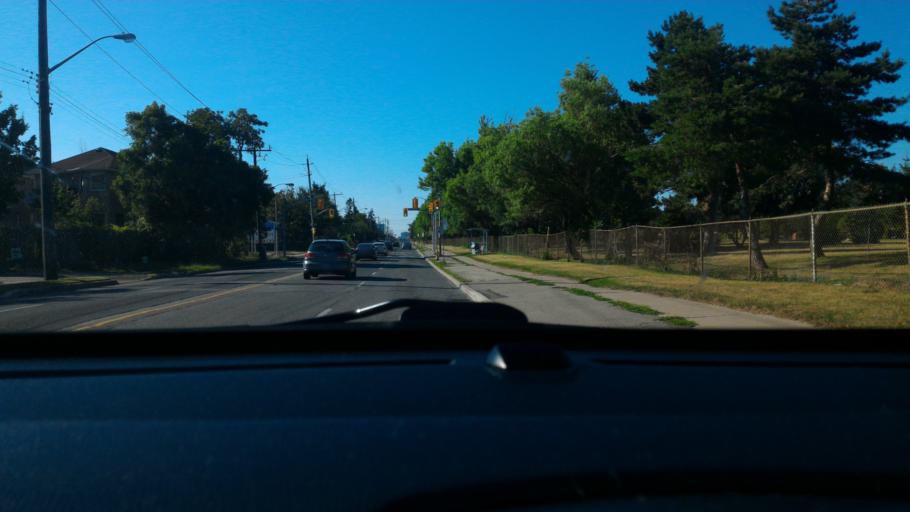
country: CA
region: Ontario
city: Scarborough
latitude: 43.7177
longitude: -79.2727
